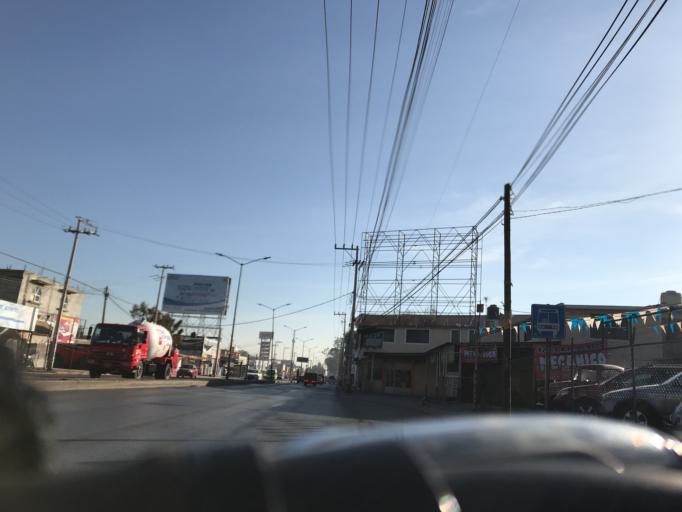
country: MX
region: Mexico
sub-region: Cuautitlan
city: La Trinidad
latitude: 19.6747
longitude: -99.1586
